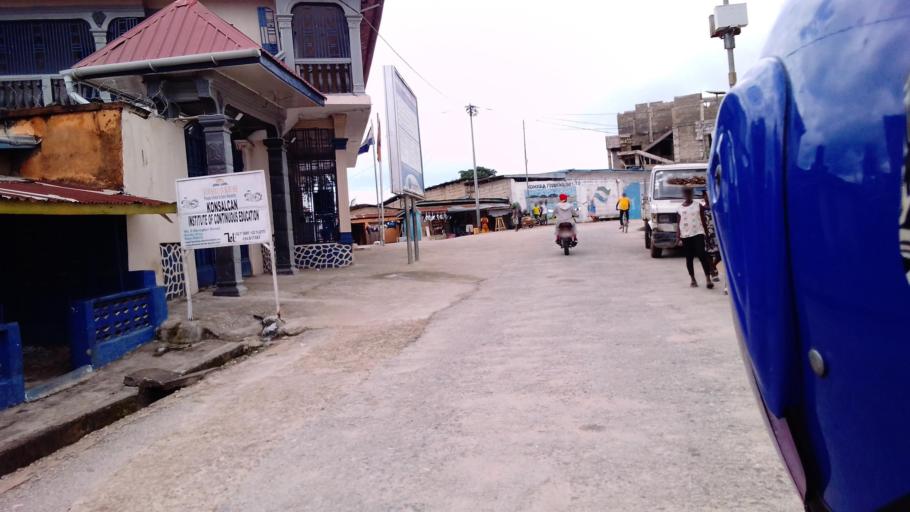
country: SL
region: Eastern Province
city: Koidu
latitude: 8.6436
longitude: -10.9765
